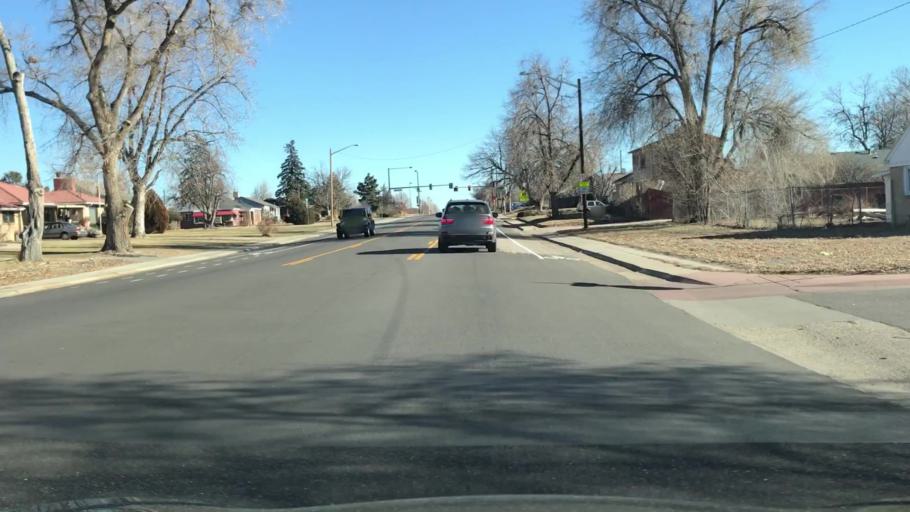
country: US
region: Colorado
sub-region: Arapahoe County
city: Glendale
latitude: 39.7474
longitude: -104.9012
